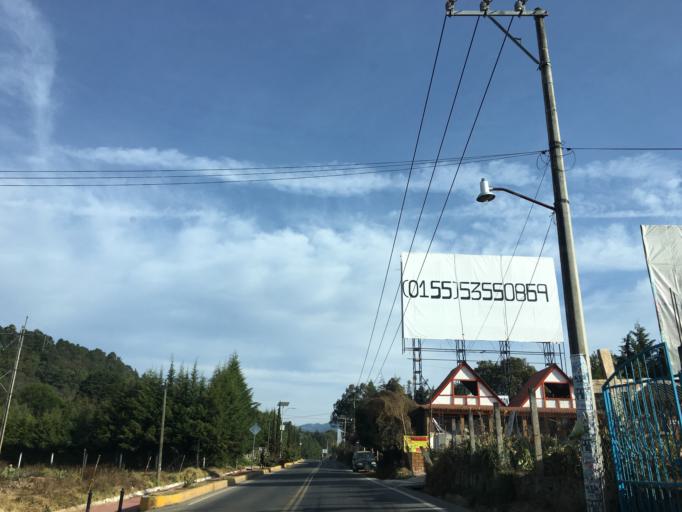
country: MX
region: Mexico
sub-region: Valle de Bravo
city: Colonia Rincon Villa del Valle
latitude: 19.1930
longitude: -100.0999
